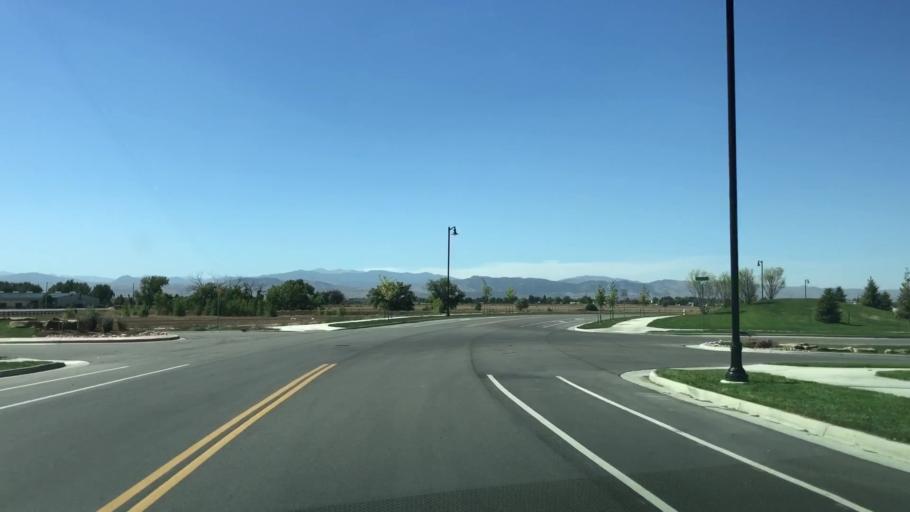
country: US
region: Colorado
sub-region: Weld County
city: Windsor
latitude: 40.5242
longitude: -104.9585
